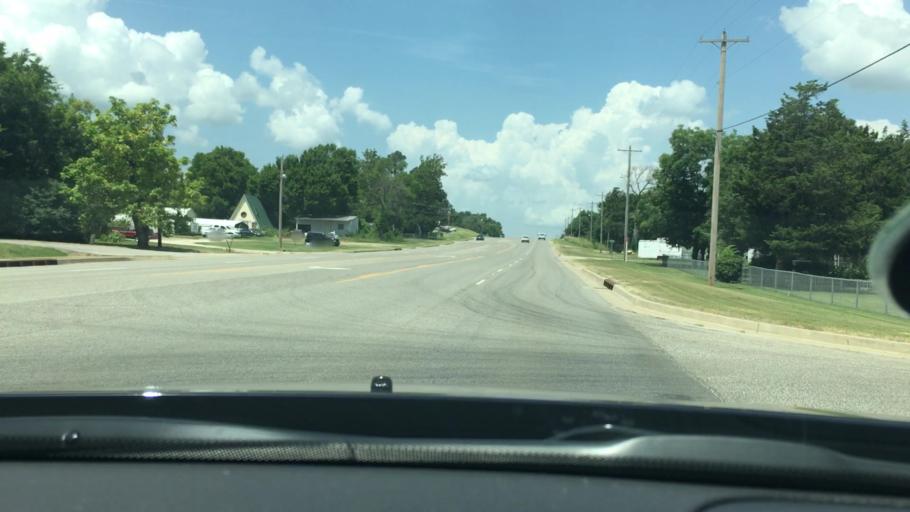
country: US
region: Oklahoma
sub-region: Marshall County
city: Oakland
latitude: 34.1000
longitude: -96.7940
